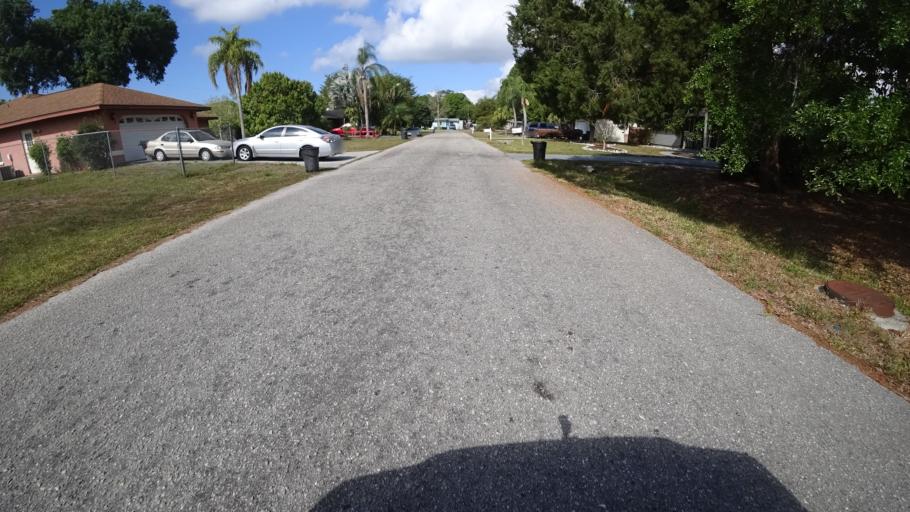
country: US
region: Florida
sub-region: Manatee County
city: Whitfield
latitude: 27.4245
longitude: -82.5648
